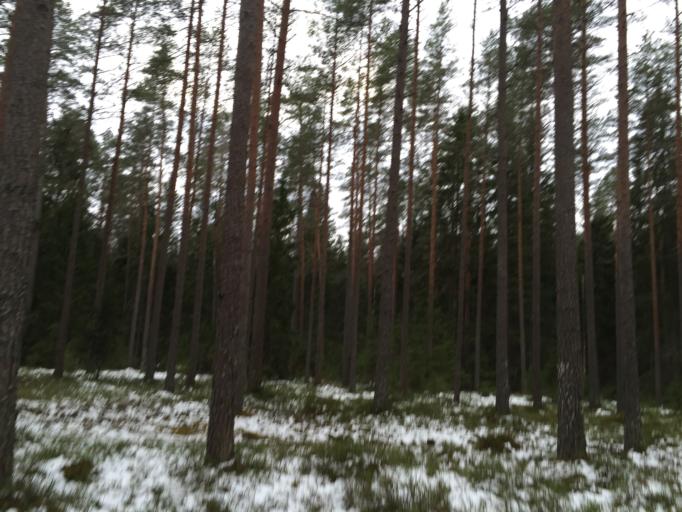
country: LV
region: Garkalne
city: Garkalne
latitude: 56.9547
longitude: 24.4639
